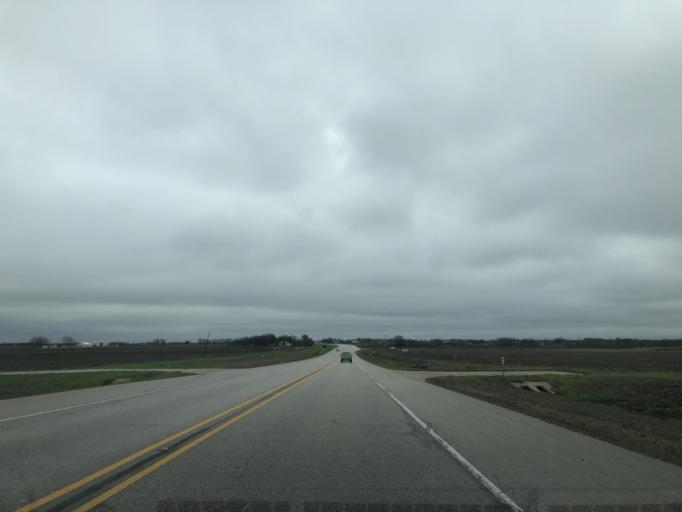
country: US
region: Texas
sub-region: Williamson County
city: Hutto
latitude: 30.6015
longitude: -97.5106
